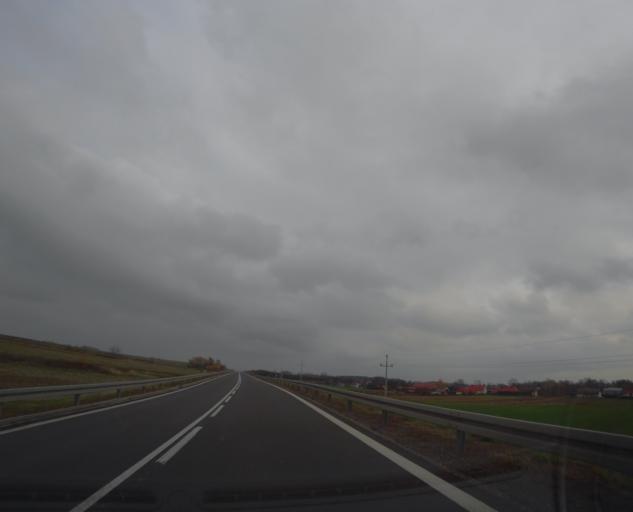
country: PL
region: Subcarpathian Voivodeship
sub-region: Powiat lezajski
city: Giedlarowa
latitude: 50.2396
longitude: 22.4196
